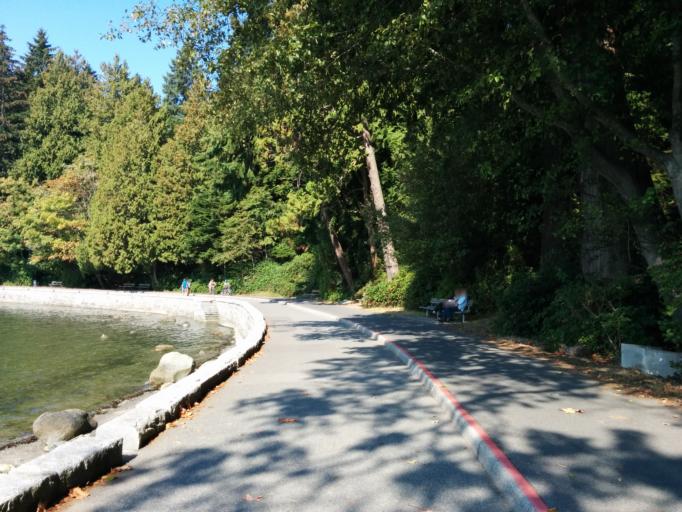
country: CA
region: British Columbia
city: West End
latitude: 49.2974
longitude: -123.1539
